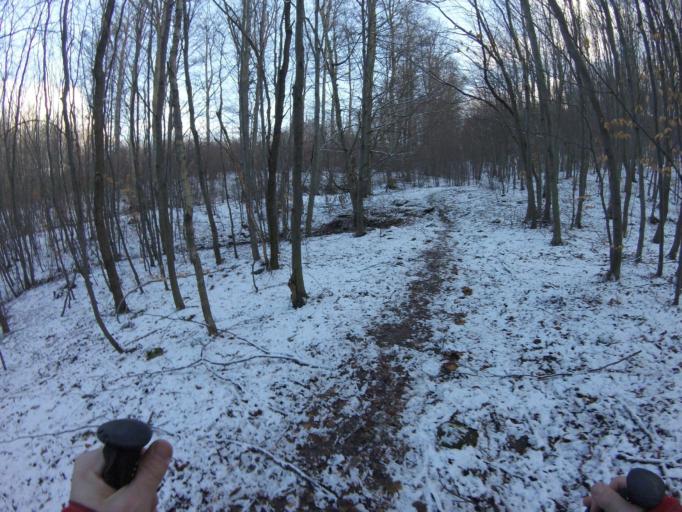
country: HU
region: Pest
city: Pilisszentkereszt
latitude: 47.7333
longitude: 18.8910
